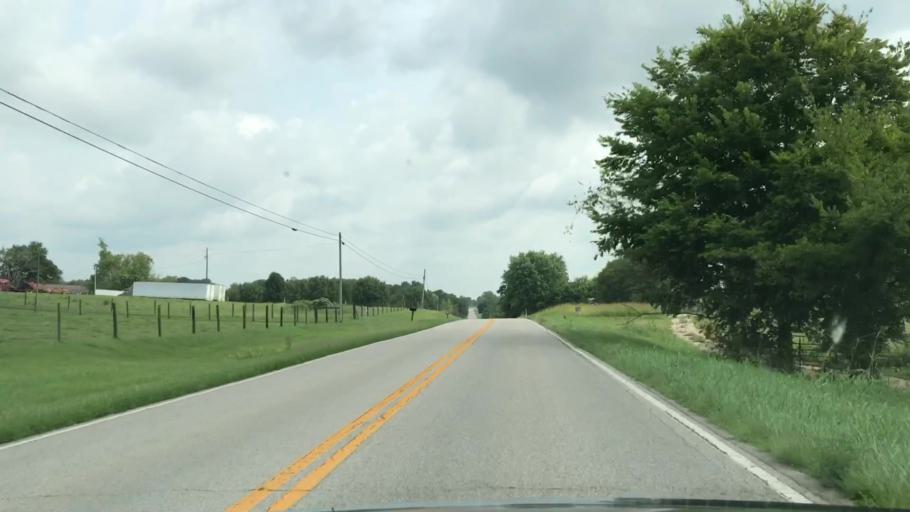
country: US
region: Kentucky
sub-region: Barren County
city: Cave City
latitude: 37.1007
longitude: -86.0050
